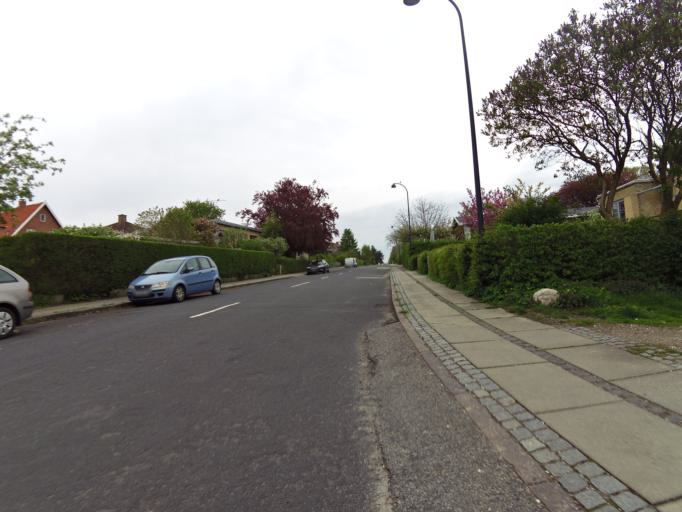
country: DK
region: Capital Region
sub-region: Lyngby-Tarbaek Kommune
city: Kongens Lyngby
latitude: 55.7296
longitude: 12.5284
